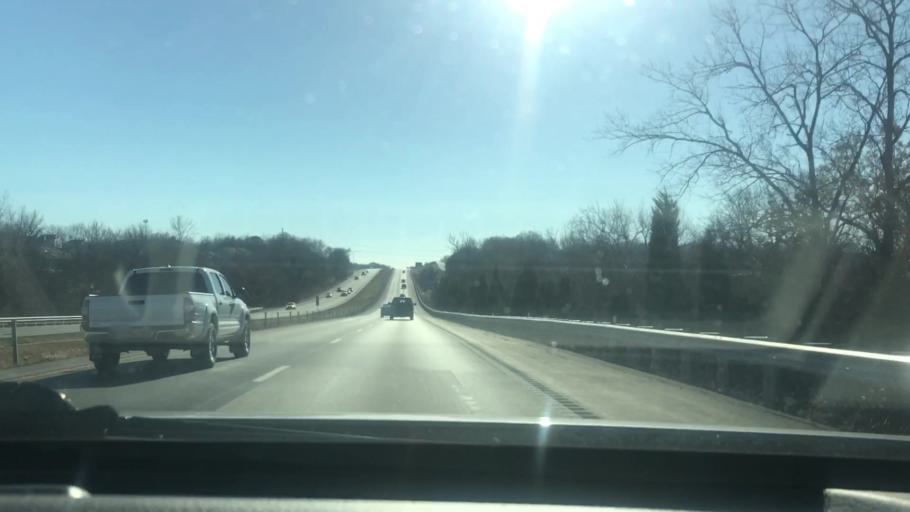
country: US
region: Missouri
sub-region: Clay County
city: Gladstone
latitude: 39.2280
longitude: -94.5887
